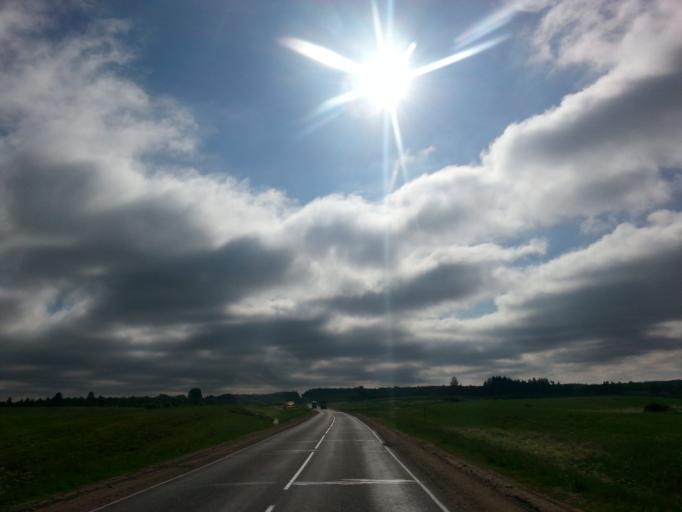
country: BY
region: Vitebsk
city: Mosar
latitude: 55.0610
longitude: 27.2349
